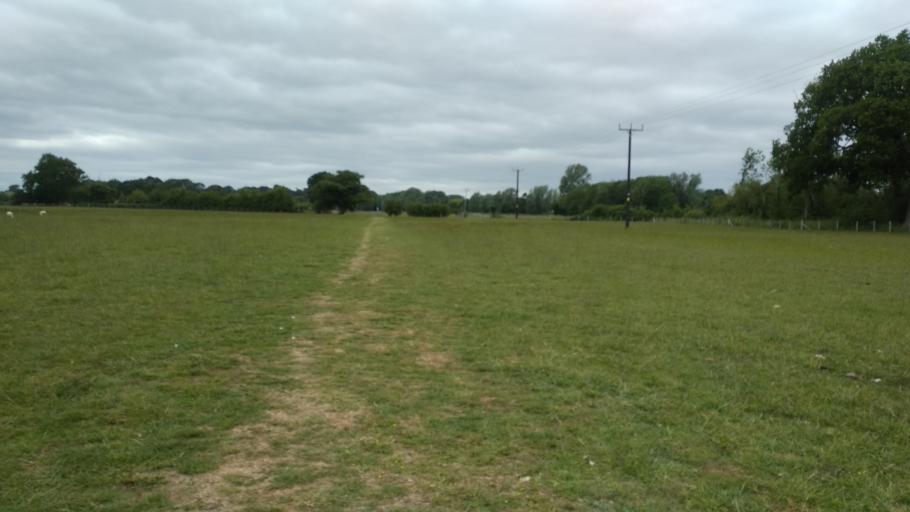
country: GB
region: England
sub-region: Kent
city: Ashford
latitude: 51.1544
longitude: 0.8306
